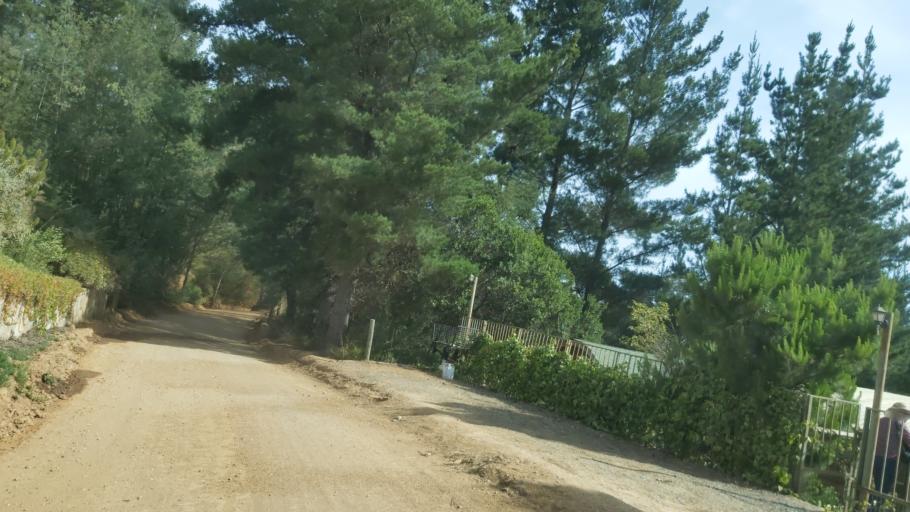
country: CL
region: Maule
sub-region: Provincia de Talca
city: Constitucion
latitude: -34.8420
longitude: -72.0404
